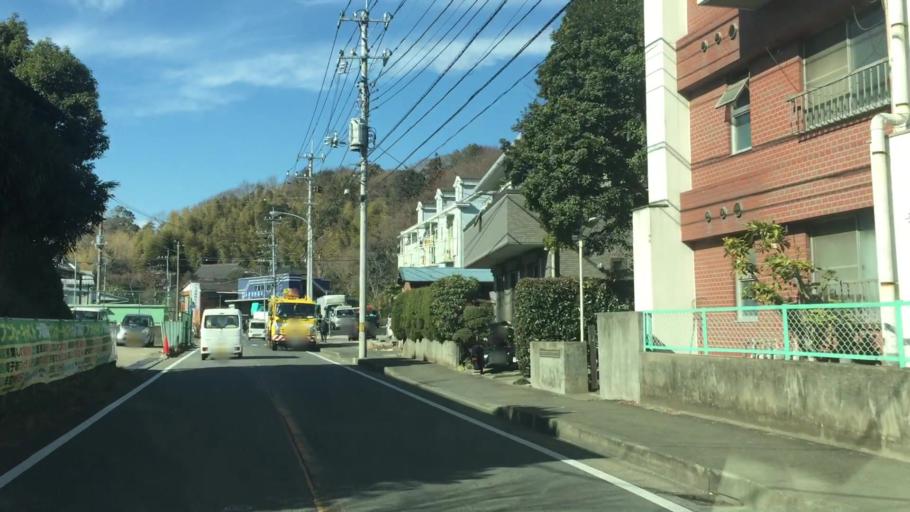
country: JP
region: Kanagawa
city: Yokohama
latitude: 35.4866
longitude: 139.5878
